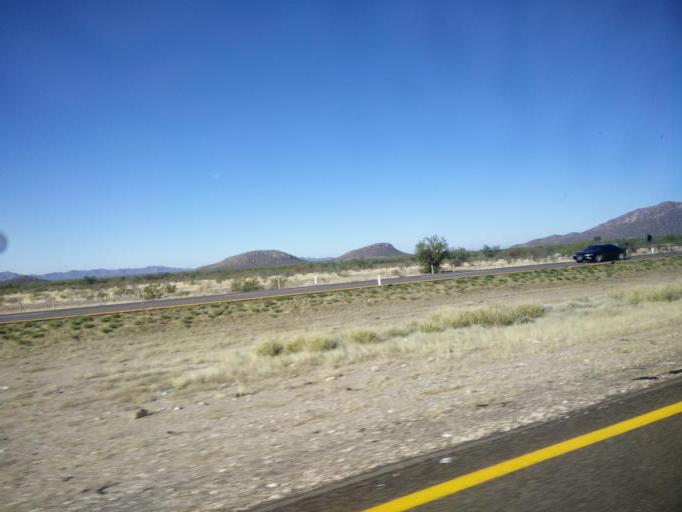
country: MX
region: Sonora
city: Hermosillo
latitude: 28.9363
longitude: -110.9561
